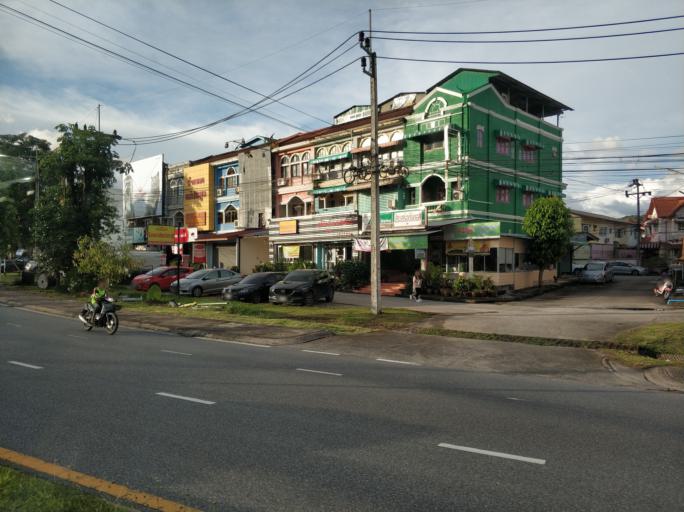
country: TH
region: Phuket
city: Kathu
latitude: 7.8990
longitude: 98.3516
